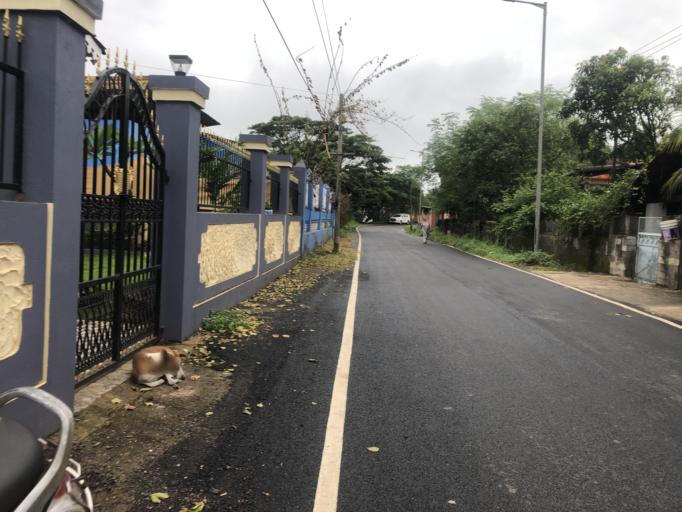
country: IN
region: Goa
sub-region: North Goa
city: Serula
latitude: 15.5348
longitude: 73.8262
